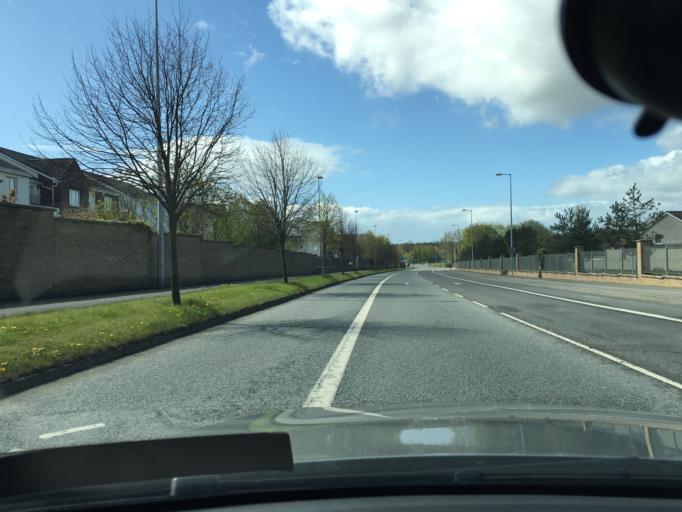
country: IE
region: Leinster
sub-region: Fingal County
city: Blanchardstown
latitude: 53.3947
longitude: -6.3756
